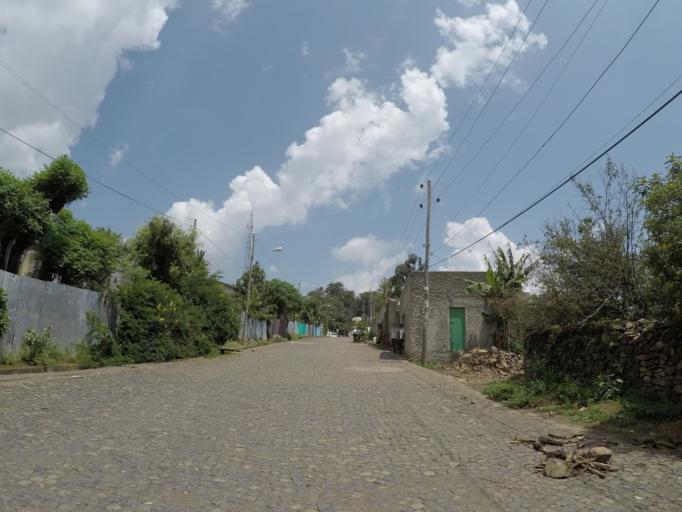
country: ET
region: Amhara
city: Gondar
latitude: 12.6136
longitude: 37.4788
